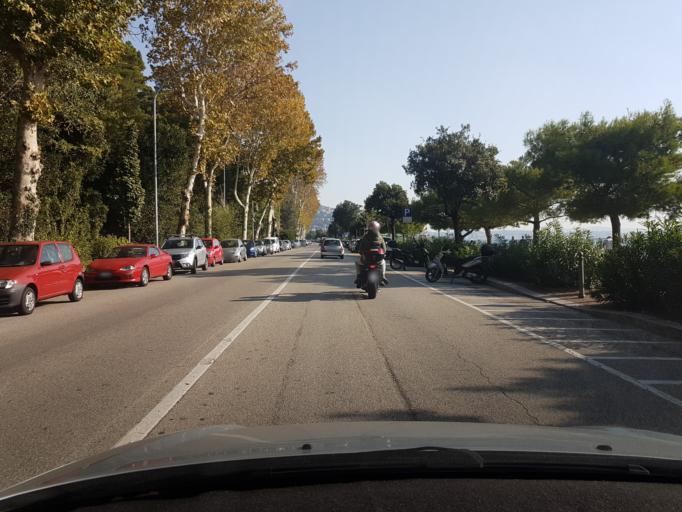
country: IT
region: Friuli Venezia Giulia
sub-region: Provincia di Trieste
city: Prosecco-Contovello
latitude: 45.6910
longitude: 13.7408
